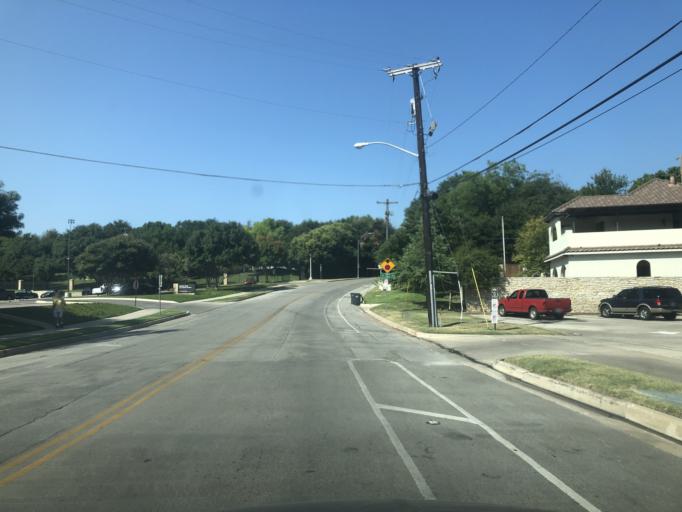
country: US
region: Texas
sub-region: Tarrant County
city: Fort Worth
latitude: 32.7067
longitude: -97.3691
